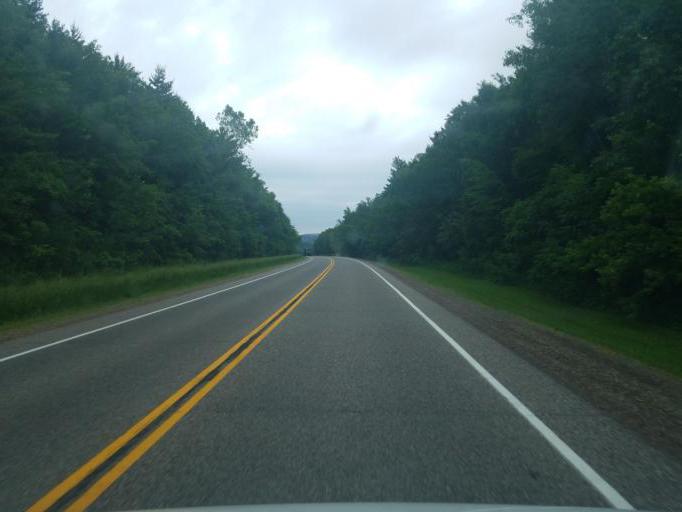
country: US
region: Wisconsin
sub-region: Juneau County
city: Elroy
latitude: 43.7804
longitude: -90.1942
